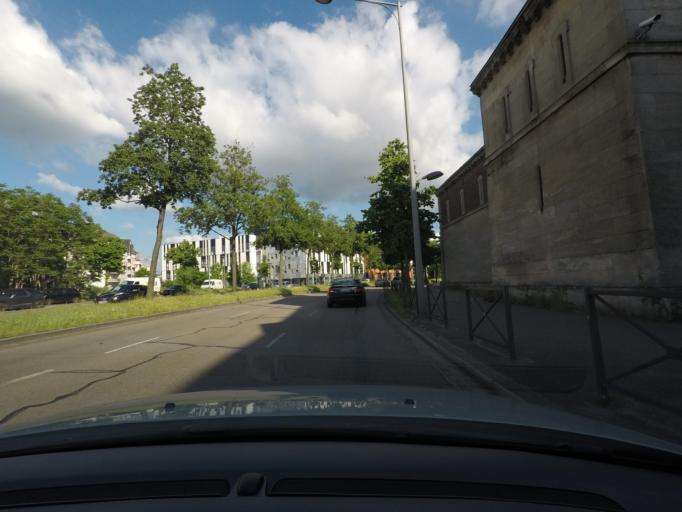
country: FR
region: Haute-Normandie
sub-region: Departement de la Seine-Maritime
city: Rouen
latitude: 49.4337
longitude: 1.0777
